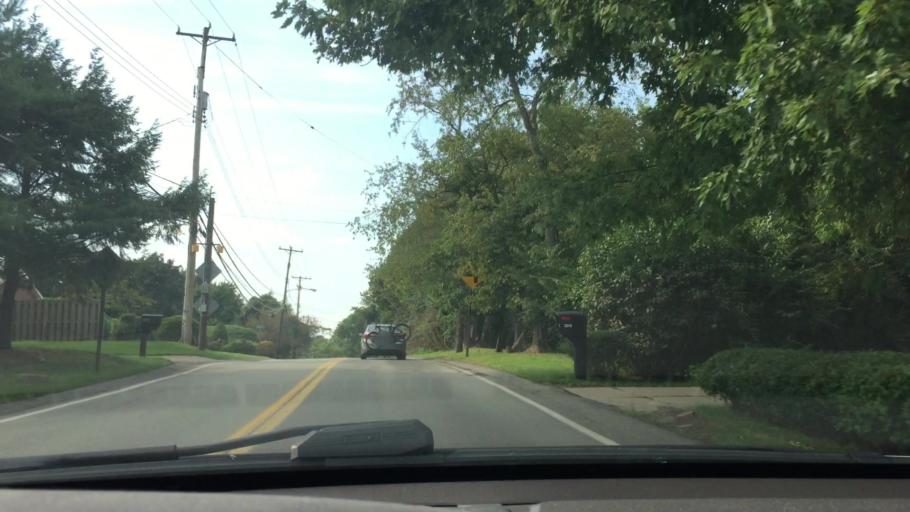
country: US
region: Pennsylvania
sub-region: Westmoreland County
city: Level Green
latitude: 40.4163
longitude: -79.7404
